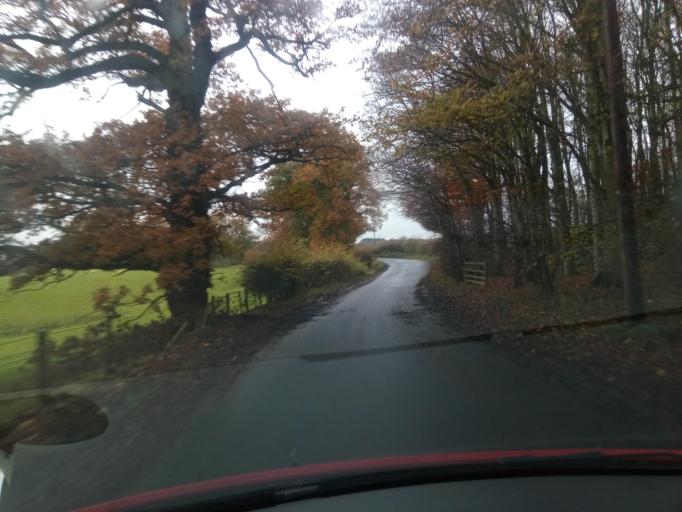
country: GB
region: Scotland
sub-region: The Scottish Borders
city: Newtown St Boswells
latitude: 55.5562
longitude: -2.6808
